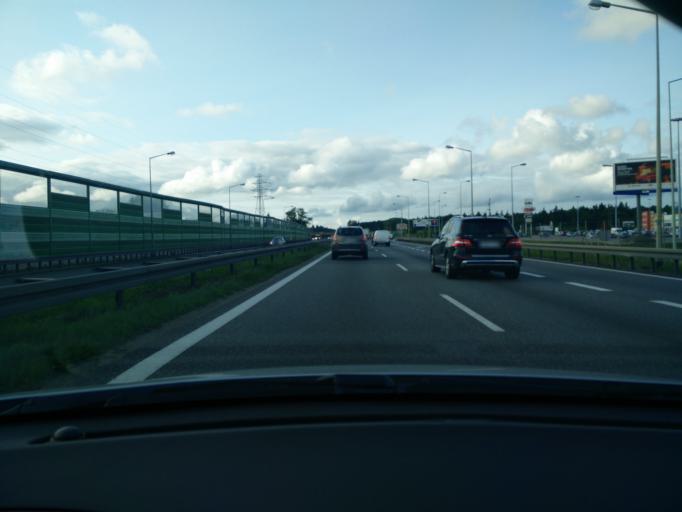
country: PL
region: Pomeranian Voivodeship
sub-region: Gdynia
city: Wielki Kack
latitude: 54.4241
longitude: 18.4877
